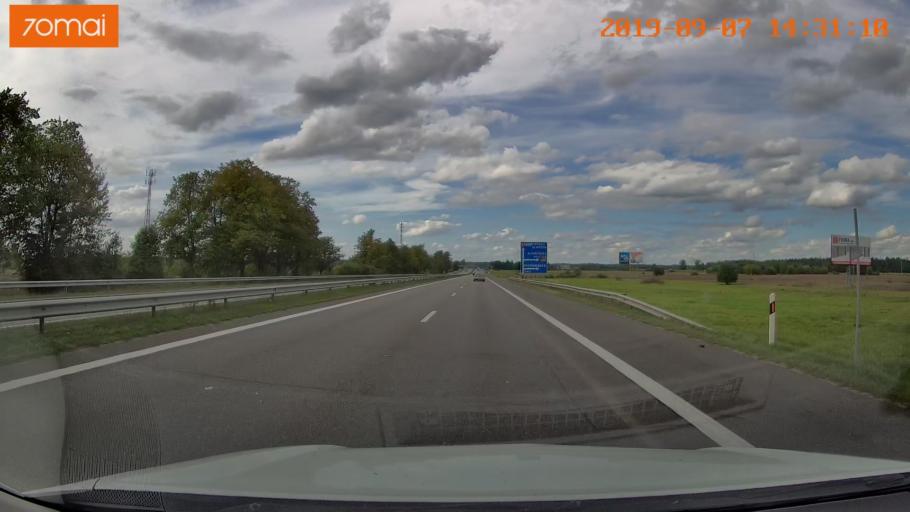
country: LT
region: Kauno apskritis
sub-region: Kauno rajonas
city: Karmelava
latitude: 54.8730
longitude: 24.2288
